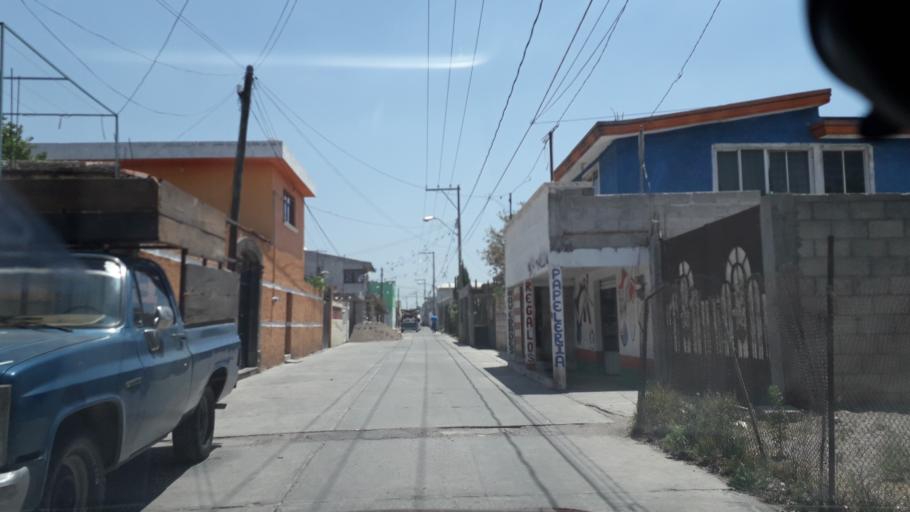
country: MX
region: Puebla
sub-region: Puebla
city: Santa Maria Xonacatepec
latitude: 19.0884
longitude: -98.1057
